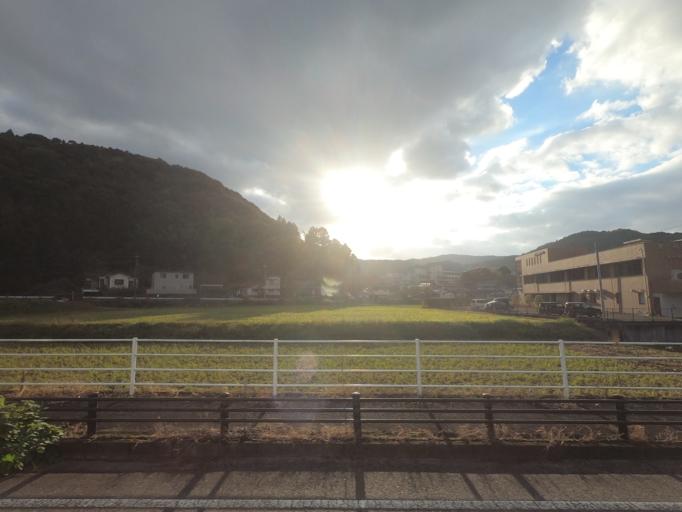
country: JP
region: Kumamoto
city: Minamata
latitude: 32.2686
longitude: 130.5046
